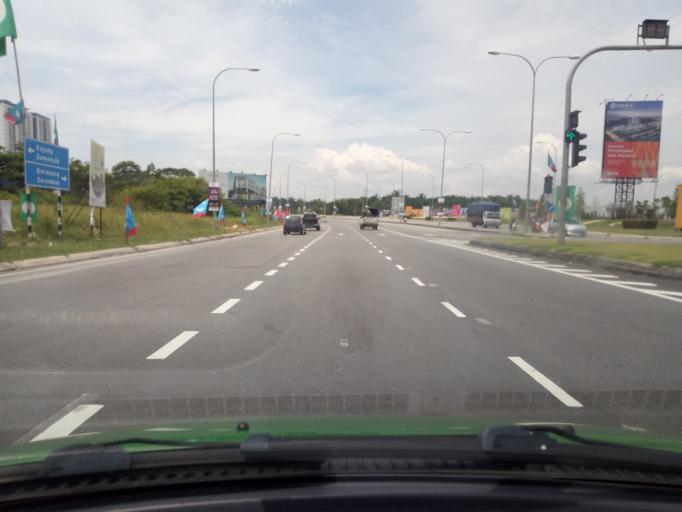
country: MY
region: Selangor
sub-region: Hulu Langat
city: Semenyih
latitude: 2.9271
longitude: 101.8571
